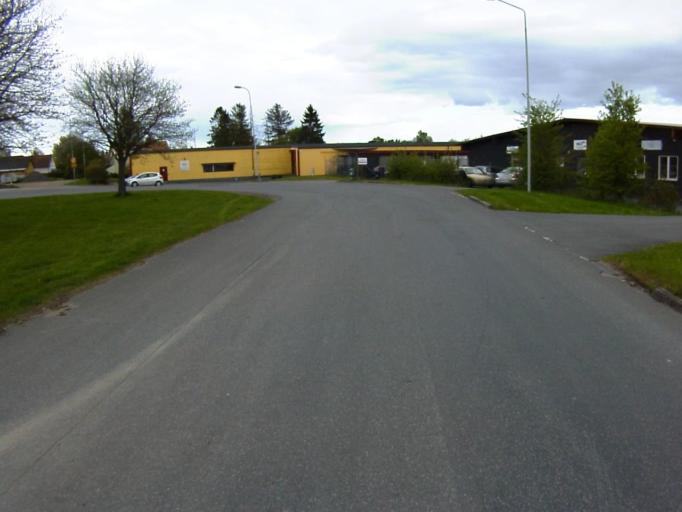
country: SE
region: Skane
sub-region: Kristianstads Kommun
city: Kristianstad
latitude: 56.0577
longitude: 14.1754
